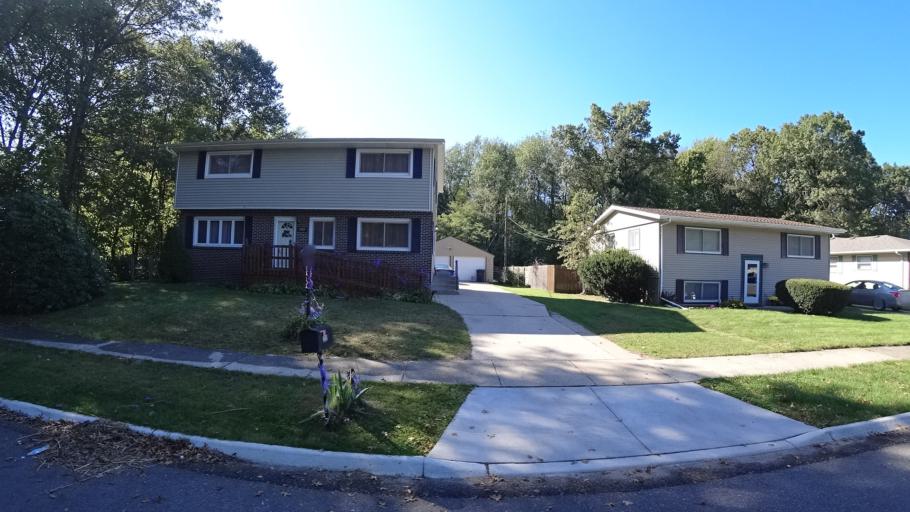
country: US
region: Indiana
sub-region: LaPorte County
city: Michigan City
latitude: 41.6879
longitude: -86.9078
